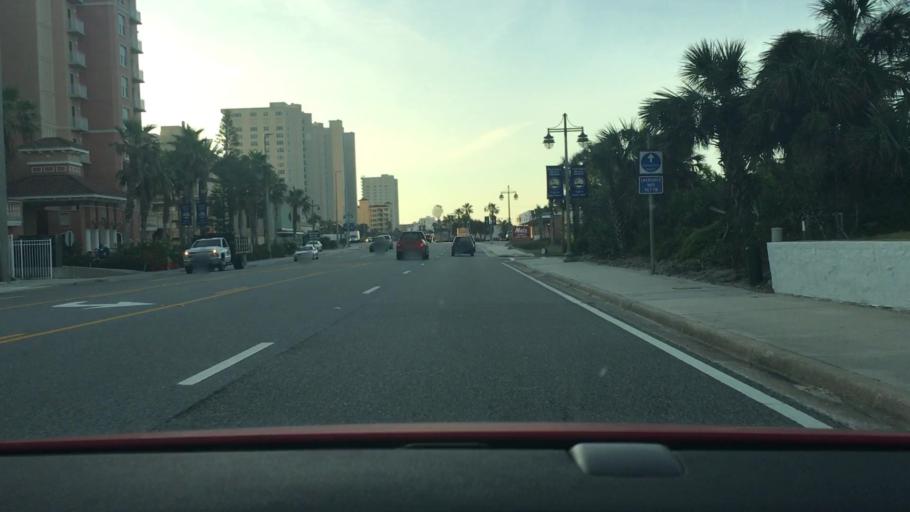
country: US
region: Florida
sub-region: Volusia County
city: Daytona Beach Shores
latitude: 29.1582
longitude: -80.9732
